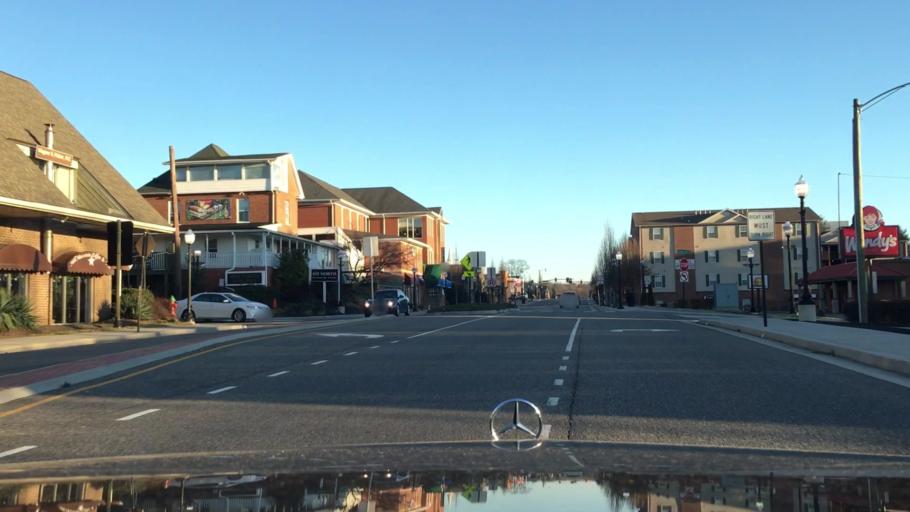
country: US
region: Virginia
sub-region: Montgomery County
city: Blacksburg
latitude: 37.2347
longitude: -80.4201
